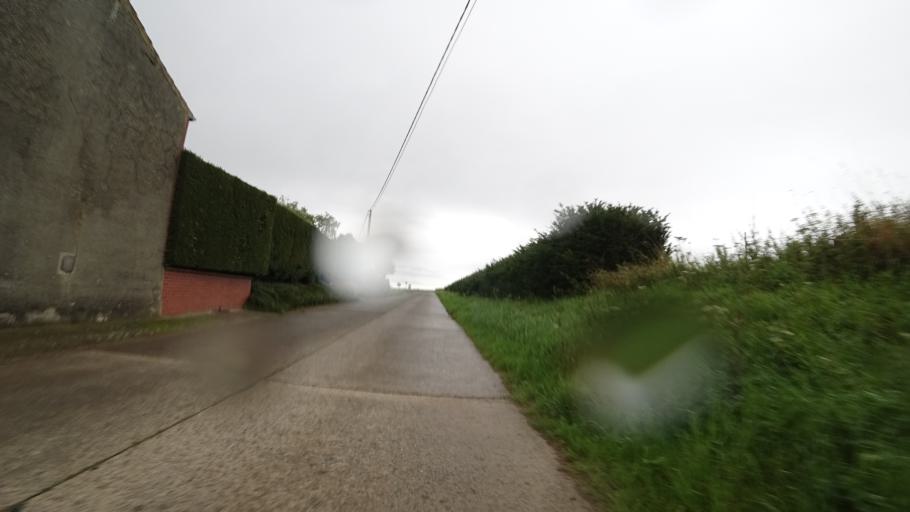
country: BE
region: Wallonia
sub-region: Province de Namur
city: Gembloux
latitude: 50.5682
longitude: 4.7354
